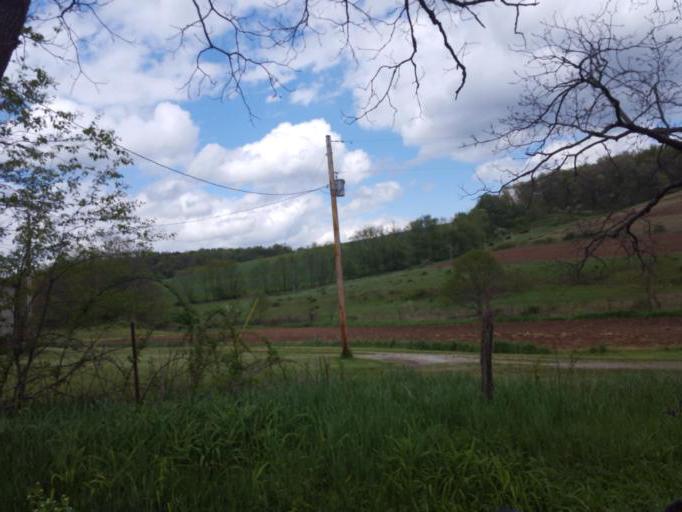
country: US
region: Ohio
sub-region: Ashland County
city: Loudonville
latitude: 40.5454
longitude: -82.2348
